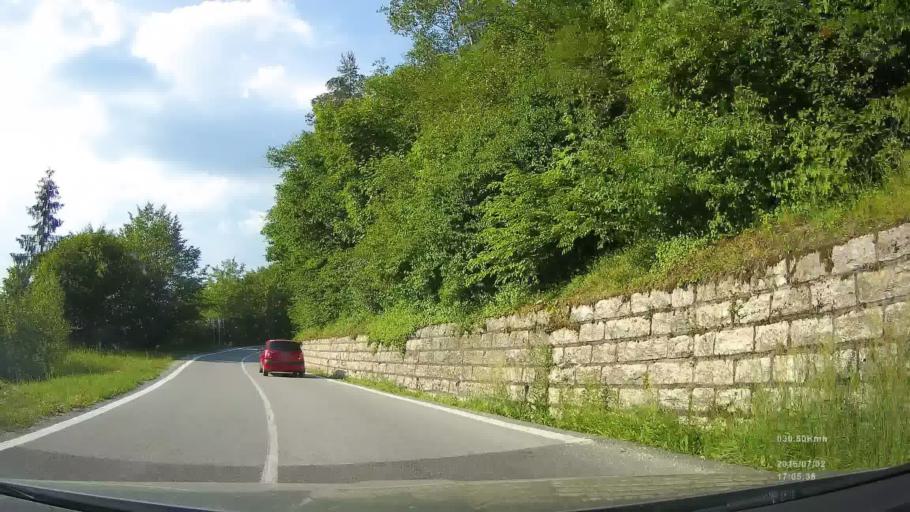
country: SK
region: Kosicky
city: Gelnica
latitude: 48.8511
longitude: 21.0155
